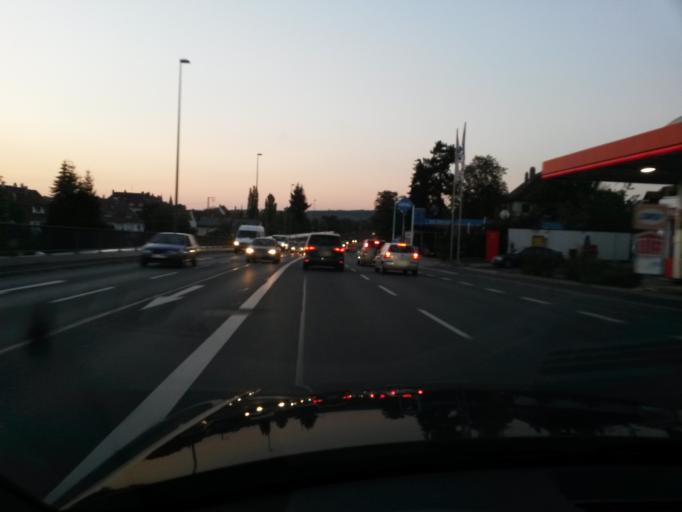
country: DE
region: Bavaria
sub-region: Regierungsbezirk Unterfranken
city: Wuerzburg
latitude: 49.7777
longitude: 9.9428
